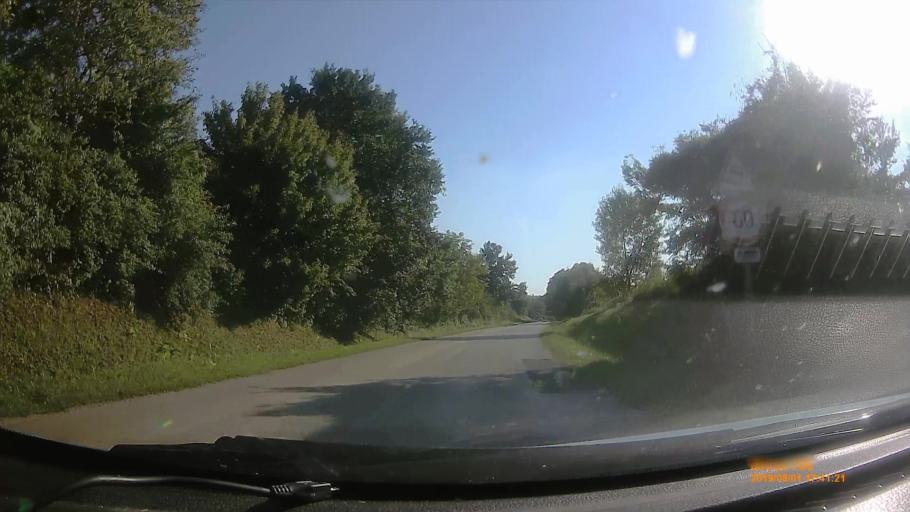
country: HU
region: Baranya
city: Komlo
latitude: 46.1928
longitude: 18.1754
